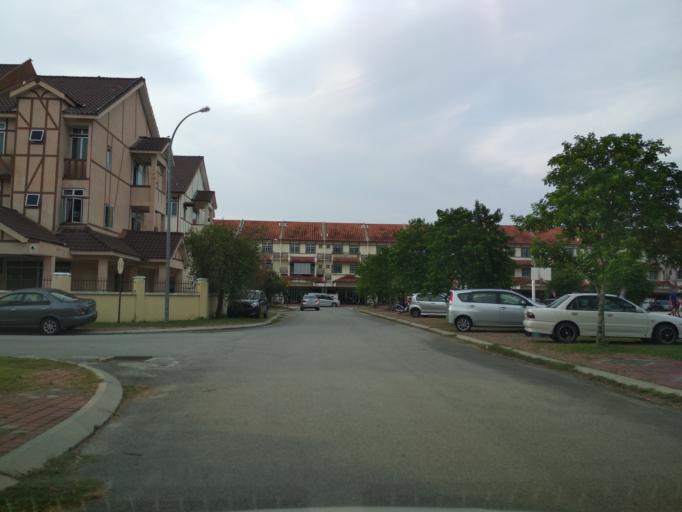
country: MY
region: Perak
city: Kampar
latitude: 4.3284
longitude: 101.1368
